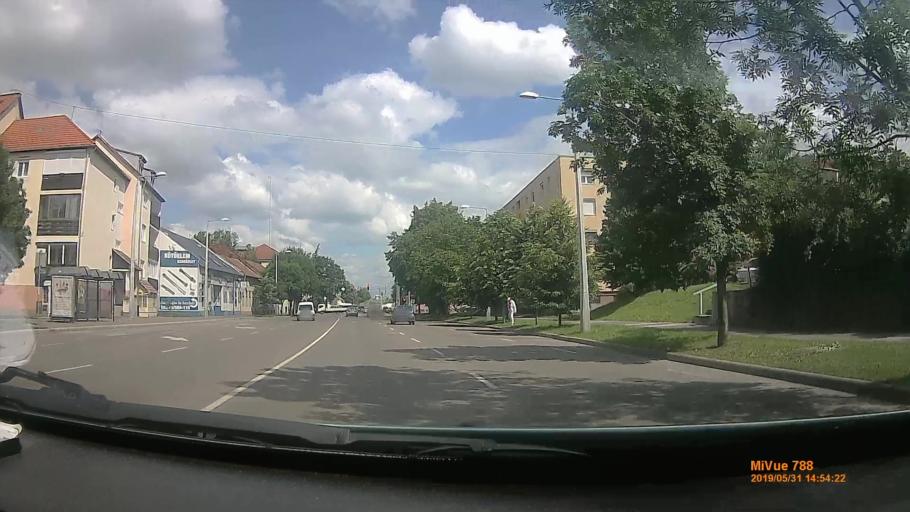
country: HU
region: Borsod-Abauj-Zemplen
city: Miskolc
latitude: 48.0995
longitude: 20.7961
